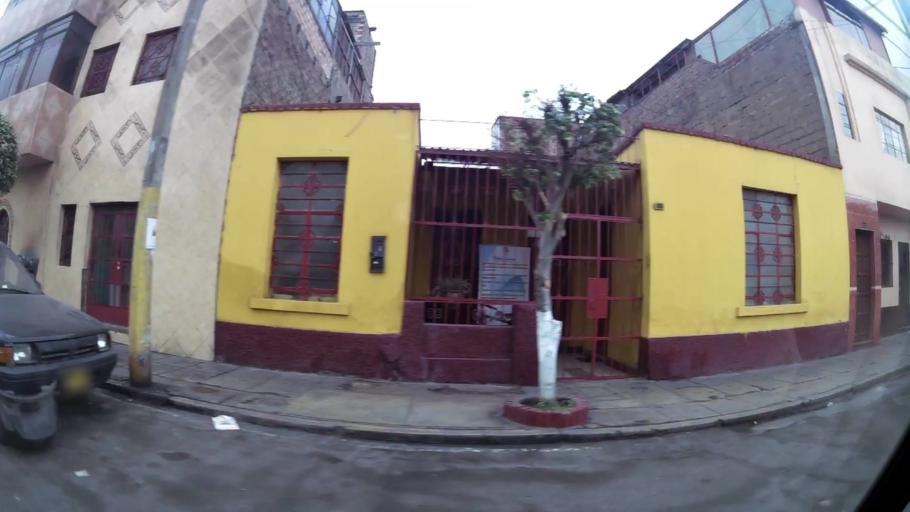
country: PE
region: Lima
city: Lima
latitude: -12.0534
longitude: -77.0512
